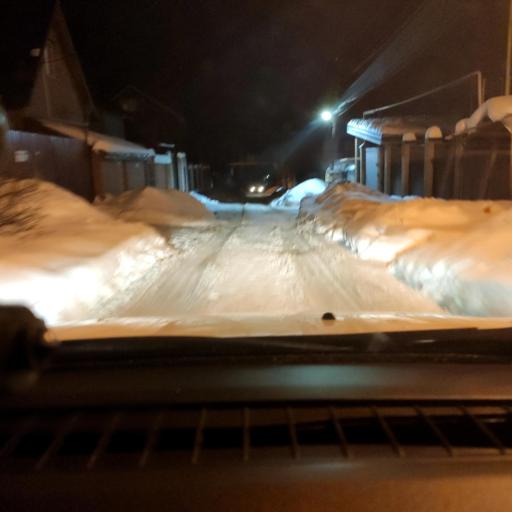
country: RU
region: Samara
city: Samara
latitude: 53.2748
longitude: 50.1991
